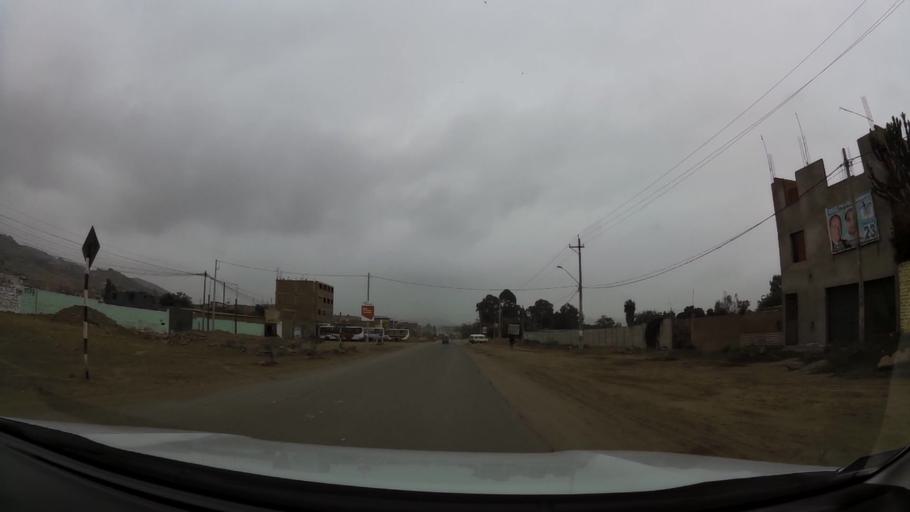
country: PE
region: Lima
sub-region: Lima
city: Cieneguilla
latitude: -12.2271
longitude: -76.9014
